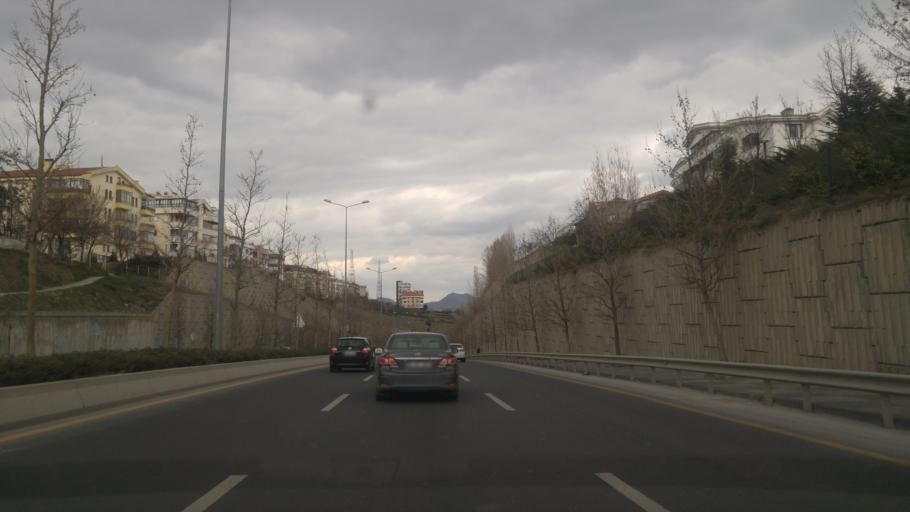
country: TR
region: Ankara
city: Cankaya
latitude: 39.8838
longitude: 32.8881
